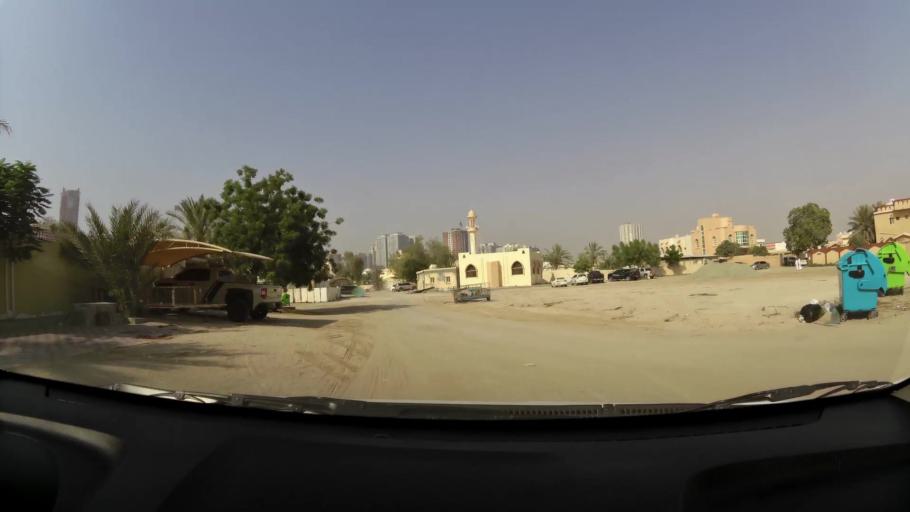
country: AE
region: Ajman
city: Ajman
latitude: 25.3867
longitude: 55.4296
